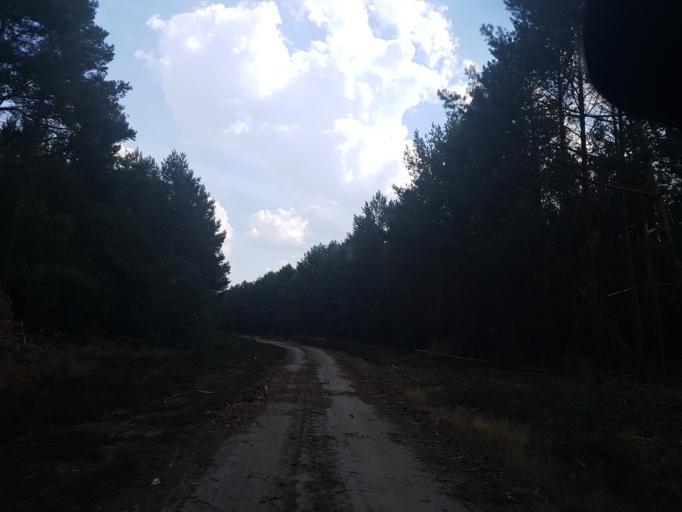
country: DE
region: Brandenburg
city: Treuenbrietzen
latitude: 52.0507
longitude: 12.8458
